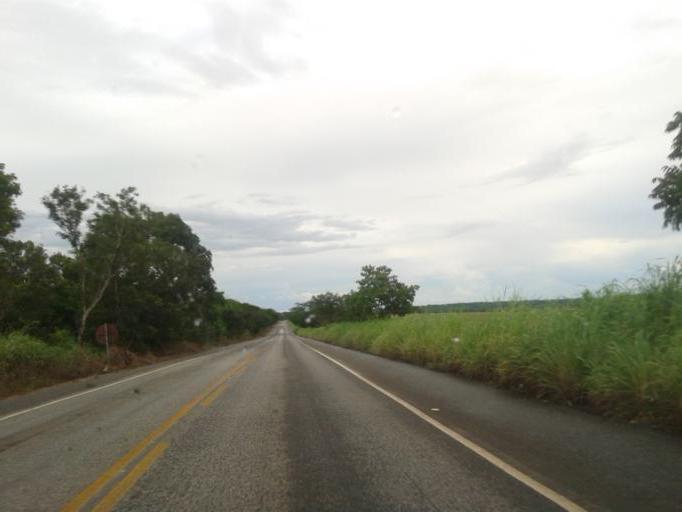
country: BR
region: Goias
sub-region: Mozarlandia
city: Mozarlandia
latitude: -14.8533
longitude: -50.5449
